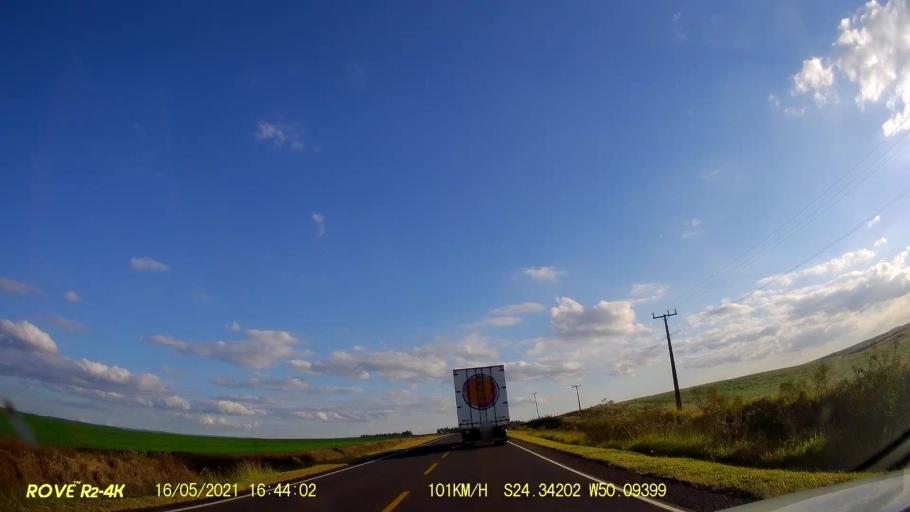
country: BR
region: Parana
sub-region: Pirai Do Sul
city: Pirai do Sul
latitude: -24.3423
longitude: -50.0940
